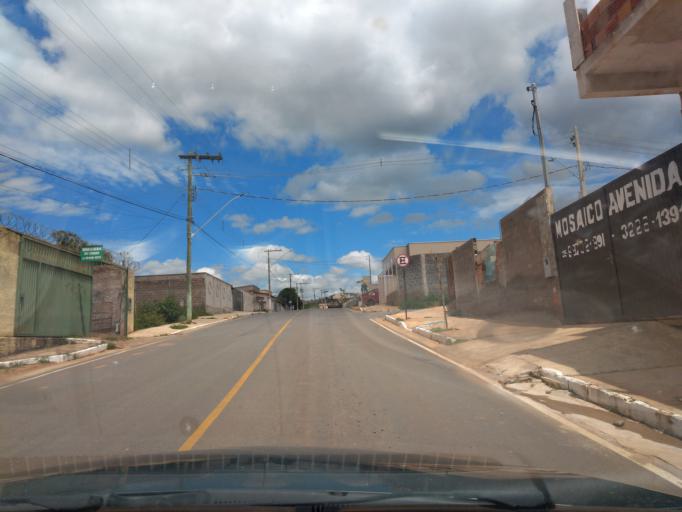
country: BR
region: Minas Gerais
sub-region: Lavras
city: Lavras
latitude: -21.5073
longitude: -44.9128
